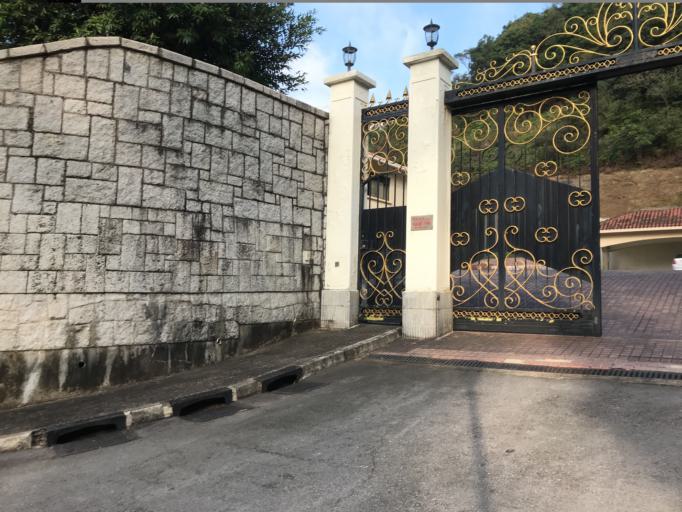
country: HK
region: Tai Po
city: Tai Po
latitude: 22.4606
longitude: 114.1573
